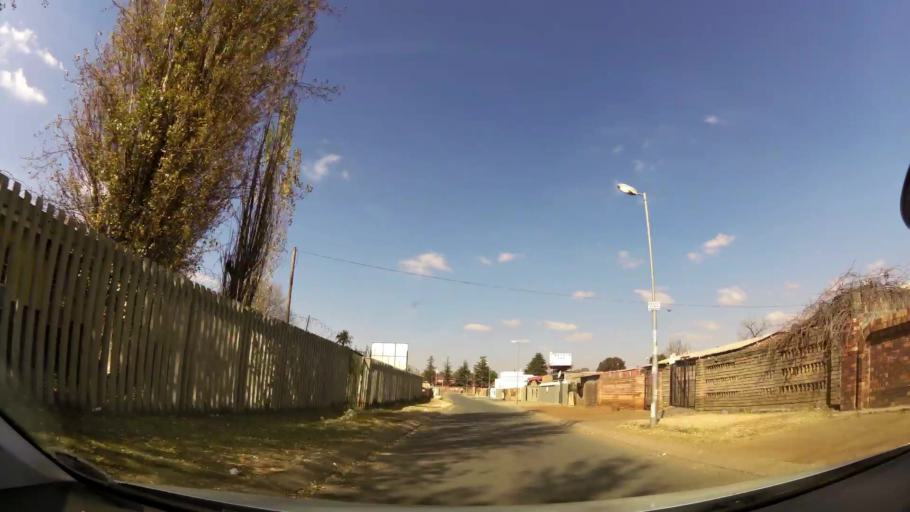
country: ZA
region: Gauteng
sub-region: City of Johannesburg Metropolitan Municipality
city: Soweto
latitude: -26.2452
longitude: 27.8827
